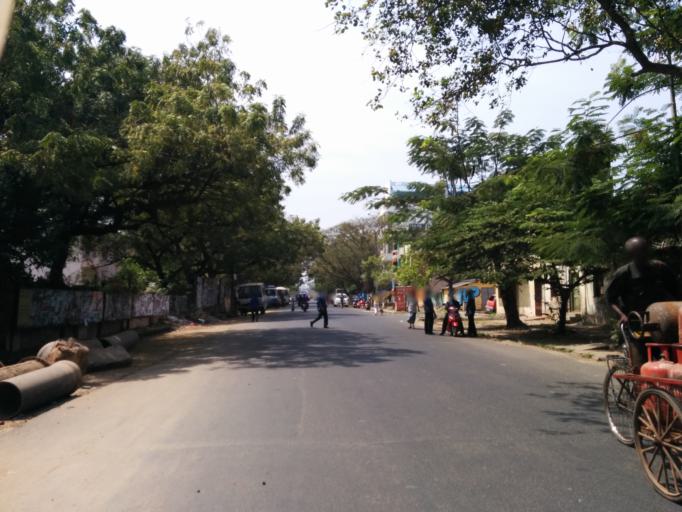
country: IN
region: Pondicherry
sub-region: Puducherry
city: Puducherry
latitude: 11.9249
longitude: 79.8301
